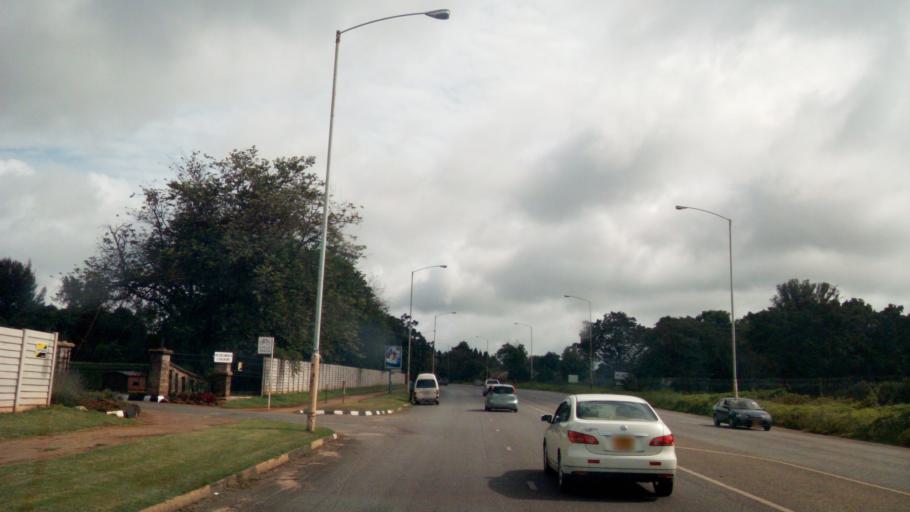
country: ZW
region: Harare
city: Harare
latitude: -17.8029
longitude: 31.0611
